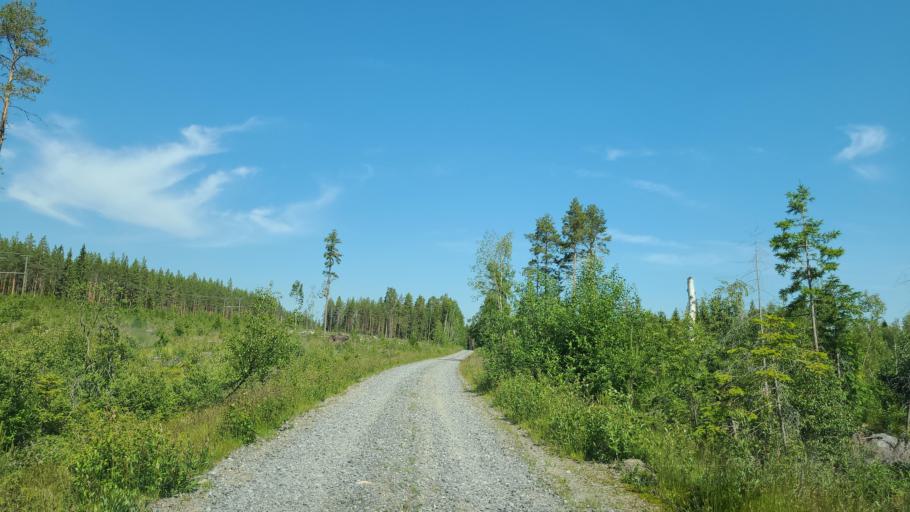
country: SE
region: Vaesterbotten
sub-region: Robertsfors Kommun
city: Robertsfors
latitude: 64.0916
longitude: 20.8357
